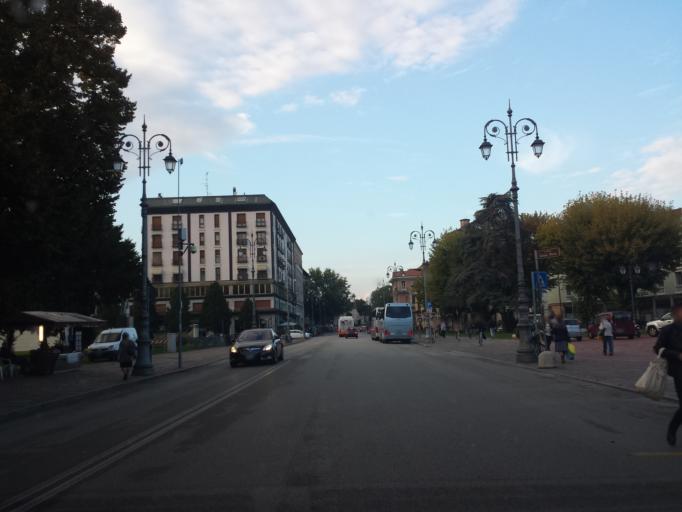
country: IT
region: Veneto
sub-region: Provincia di Vicenza
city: Vicenza
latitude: 45.5437
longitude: 11.5405
